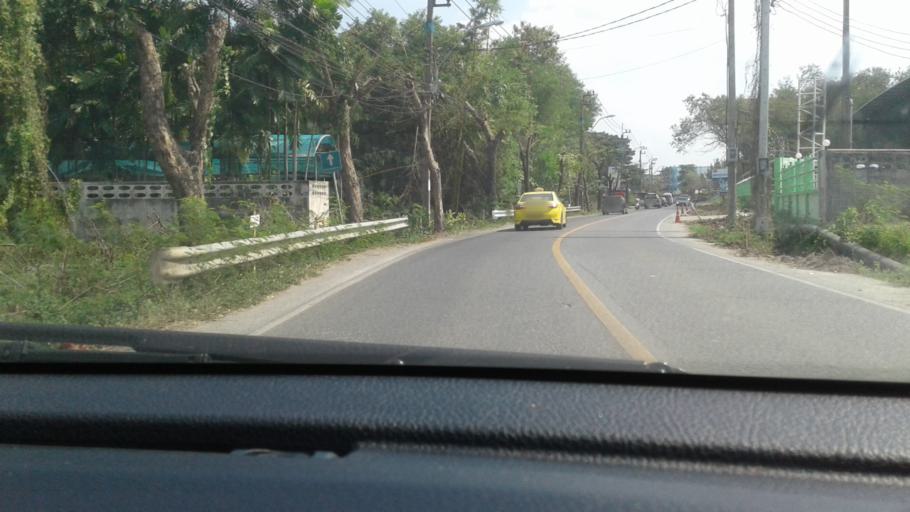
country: TH
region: Bangkok
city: Thawi Watthana
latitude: 13.7975
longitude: 100.3826
